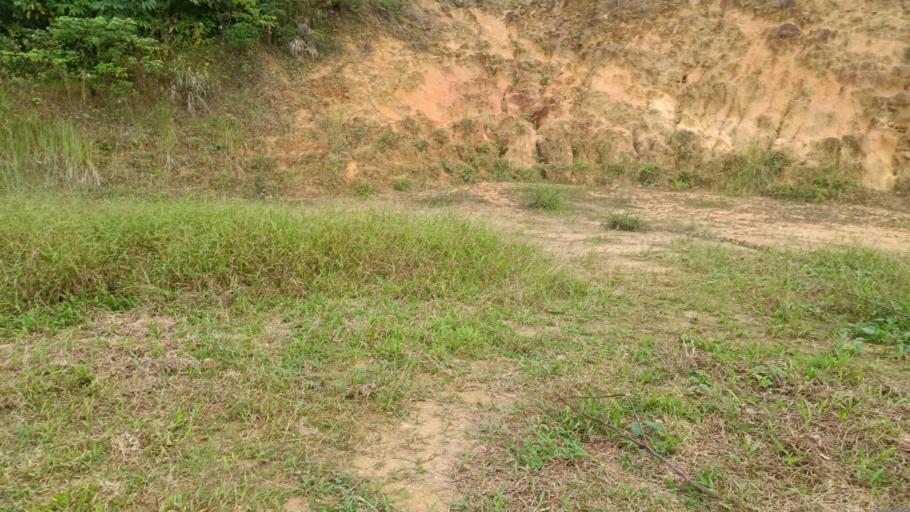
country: MY
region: Penang
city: Nibong Tebal
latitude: 5.2318
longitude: 100.5126
